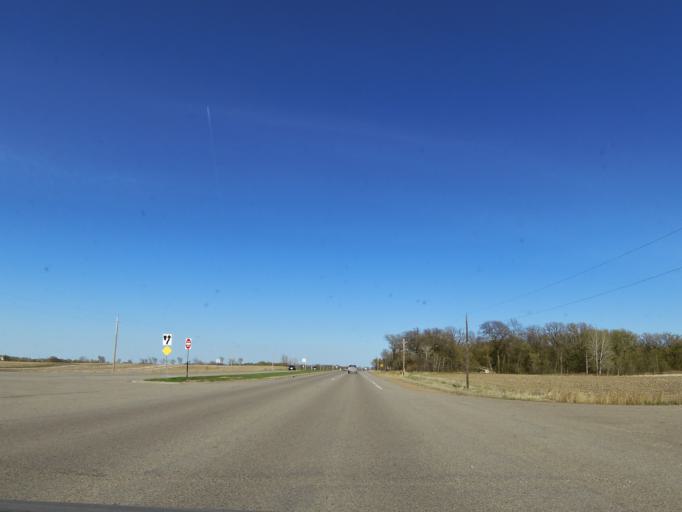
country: US
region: Minnesota
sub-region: Scott County
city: Elko New Market
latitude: 44.5731
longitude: -93.3240
